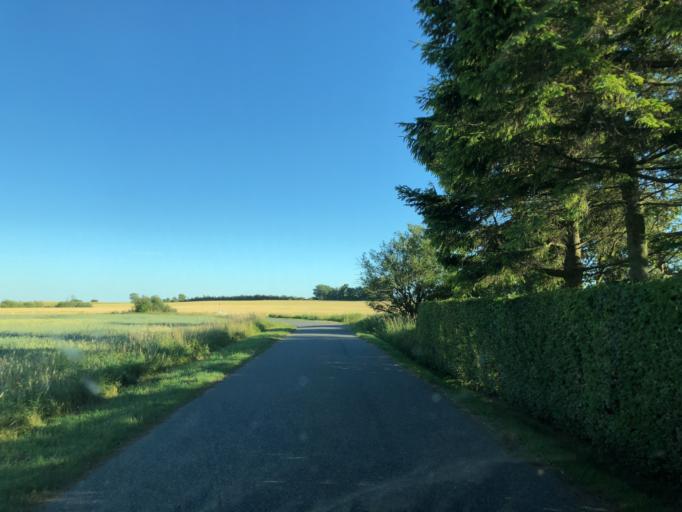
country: DK
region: Central Jutland
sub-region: Horsens Kommune
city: Horsens
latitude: 55.9705
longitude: 9.8074
